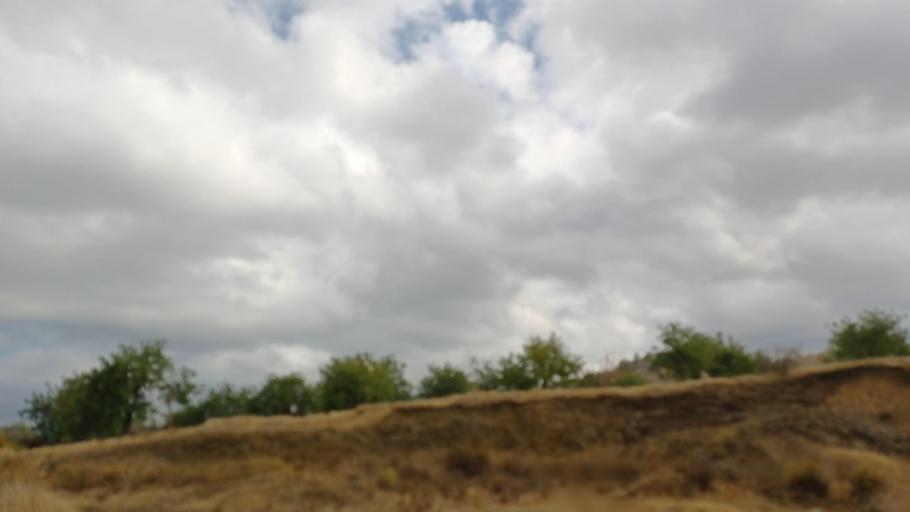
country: CY
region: Pafos
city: Polis
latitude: 35.0013
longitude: 32.4978
